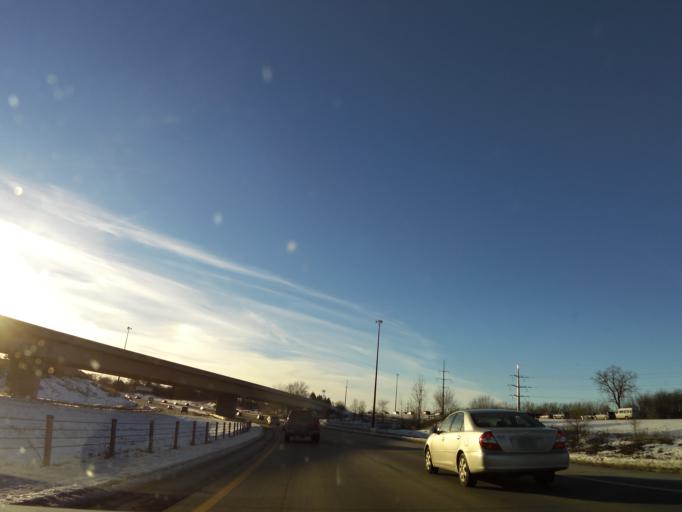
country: US
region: Minnesota
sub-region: Hennepin County
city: Eden Prairie
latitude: 44.8616
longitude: -93.4720
